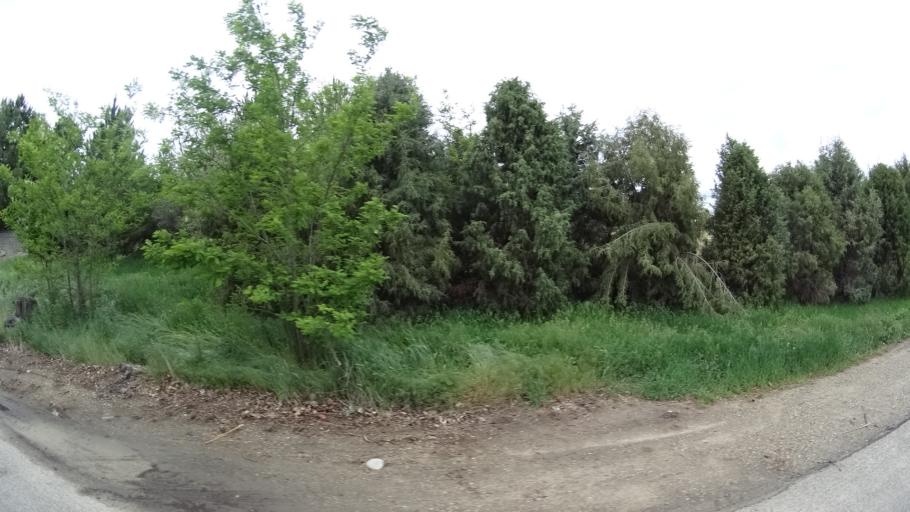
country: US
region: Idaho
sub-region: Ada County
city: Eagle
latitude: 43.7065
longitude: -116.3754
